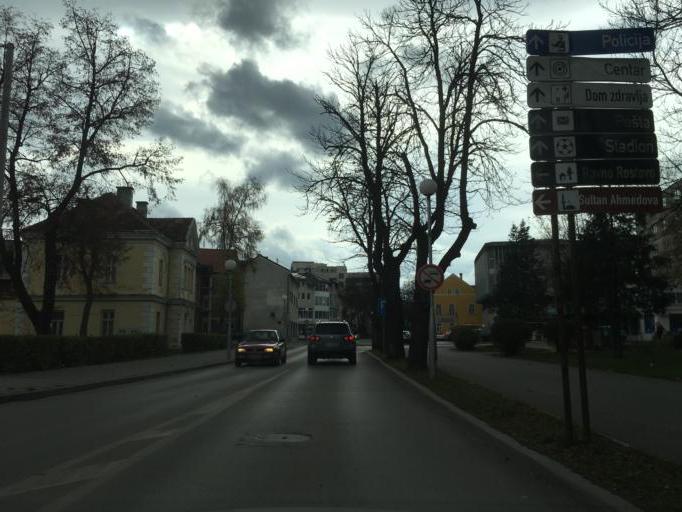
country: BA
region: Federation of Bosnia and Herzegovina
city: Bugojno
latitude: 44.0563
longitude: 17.4480
